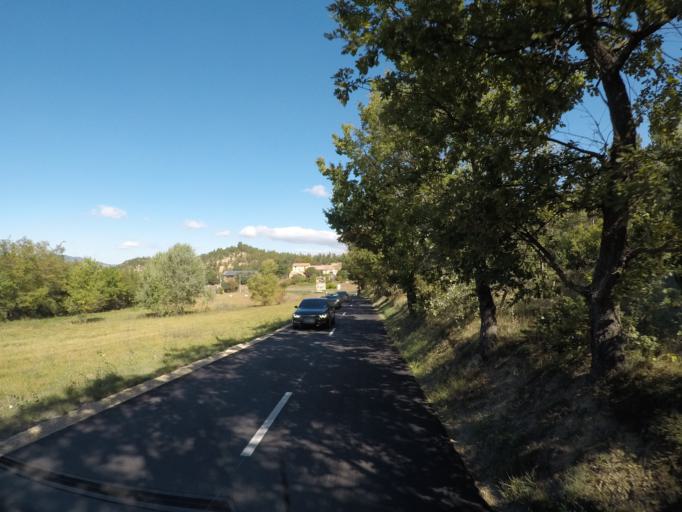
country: FR
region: Provence-Alpes-Cote d'Azur
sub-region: Departement des Alpes-de-Haute-Provence
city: Mallemoisson
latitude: 44.0192
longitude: 6.1791
